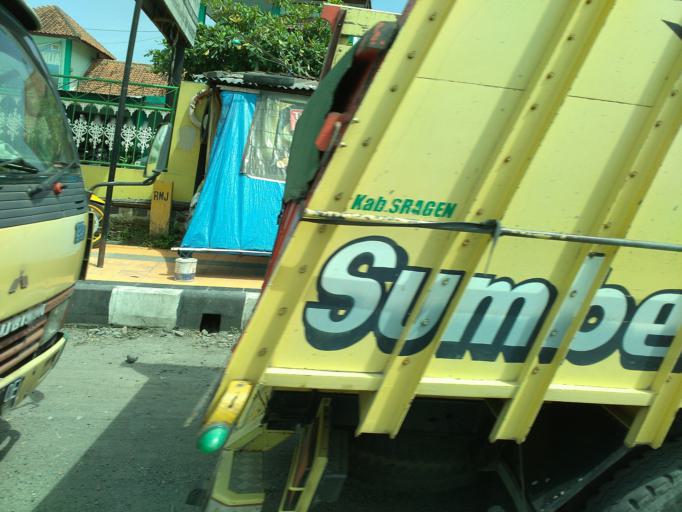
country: ID
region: Central Java
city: Wedi
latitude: -7.7177
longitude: 110.5818
